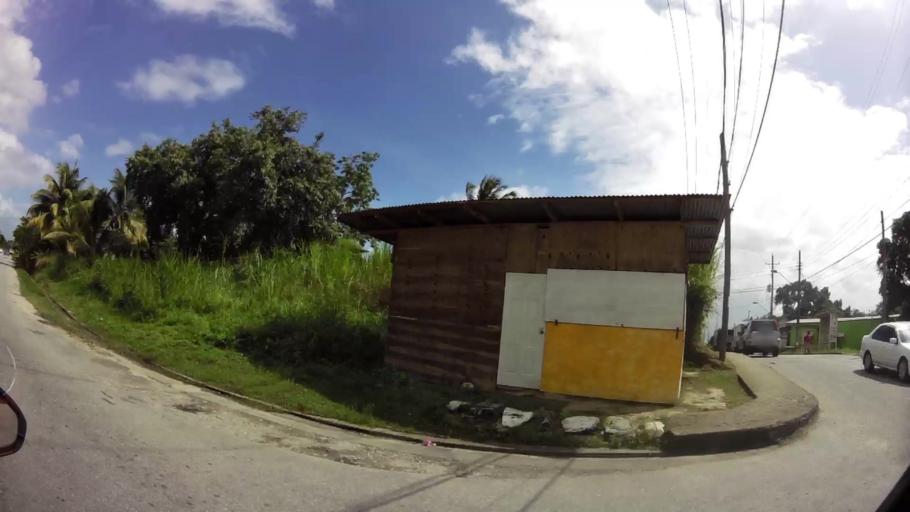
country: TT
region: Borough of Arima
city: Arima
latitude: 10.6276
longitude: -61.2673
